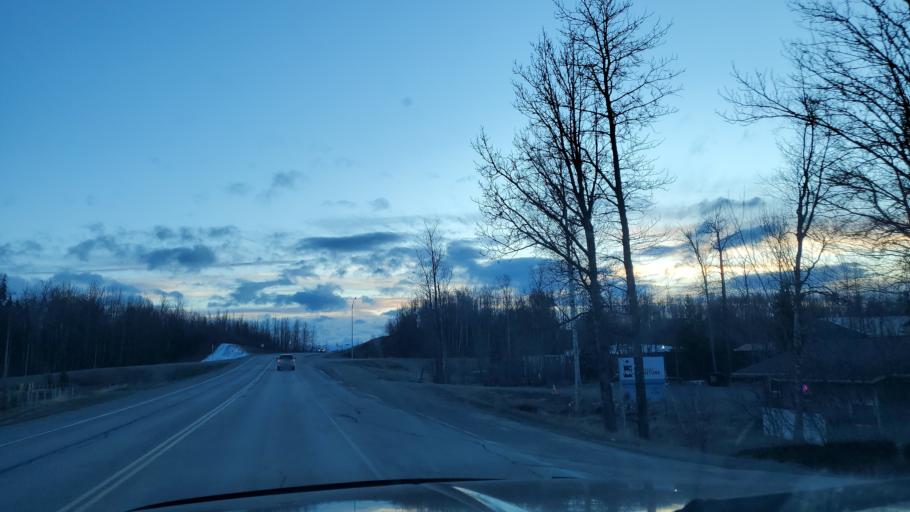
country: US
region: Alaska
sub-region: Matanuska-Susitna Borough
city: Wasilla
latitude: 61.5769
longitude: -149.4415
